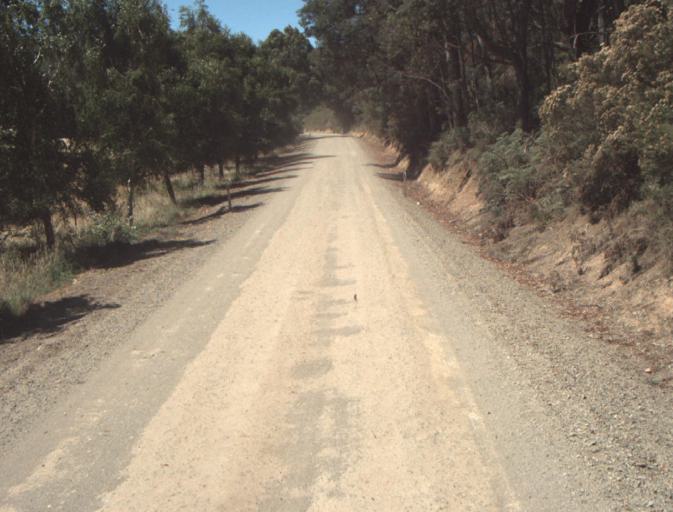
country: AU
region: Tasmania
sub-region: Dorset
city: Scottsdale
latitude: -41.2946
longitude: 147.4019
